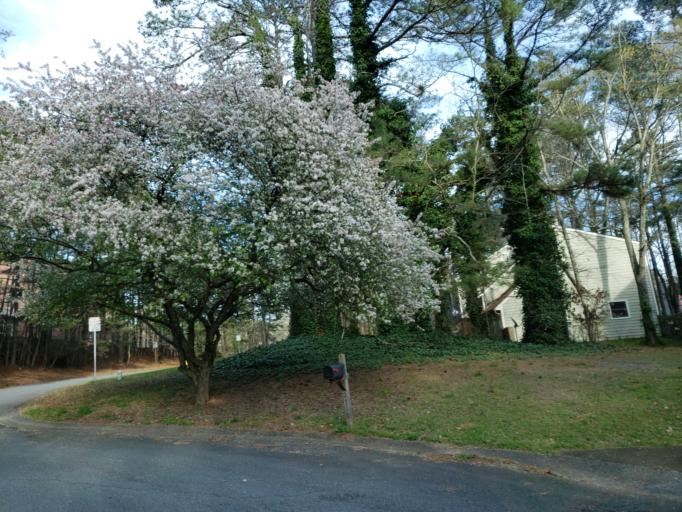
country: US
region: Georgia
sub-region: Cobb County
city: Marietta
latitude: 33.9577
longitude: -84.4794
